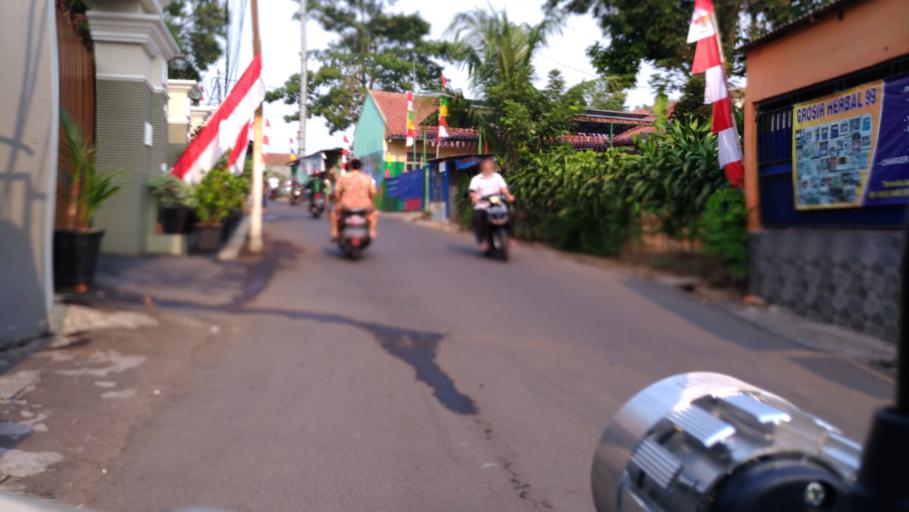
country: ID
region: West Java
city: Depok
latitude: -6.3516
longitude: 106.8710
